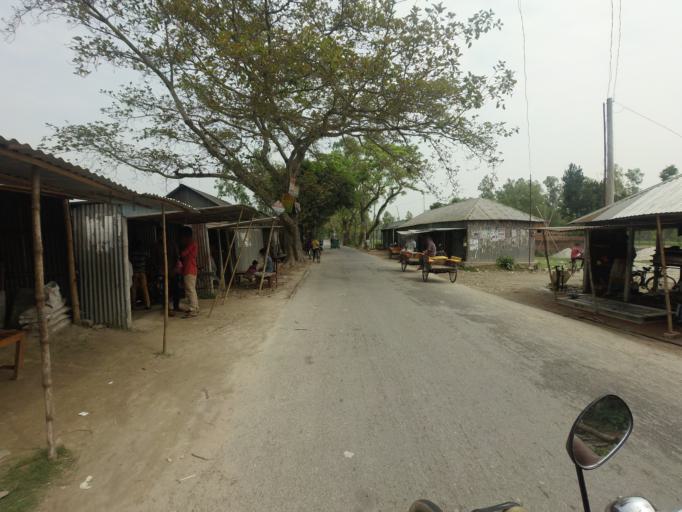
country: BD
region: Rajshahi
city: Sirajganj
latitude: 24.3838
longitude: 89.6833
